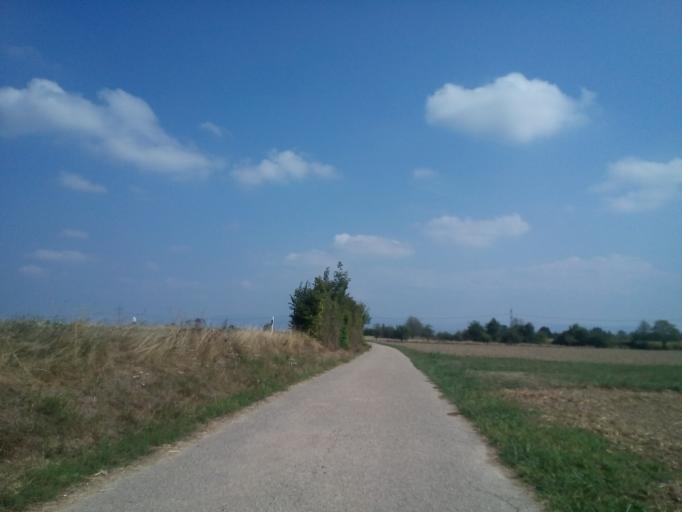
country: DE
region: Baden-Wuerttemberg
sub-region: Freiburg Region
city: Rheinau
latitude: 48.6328
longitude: 7.9155
